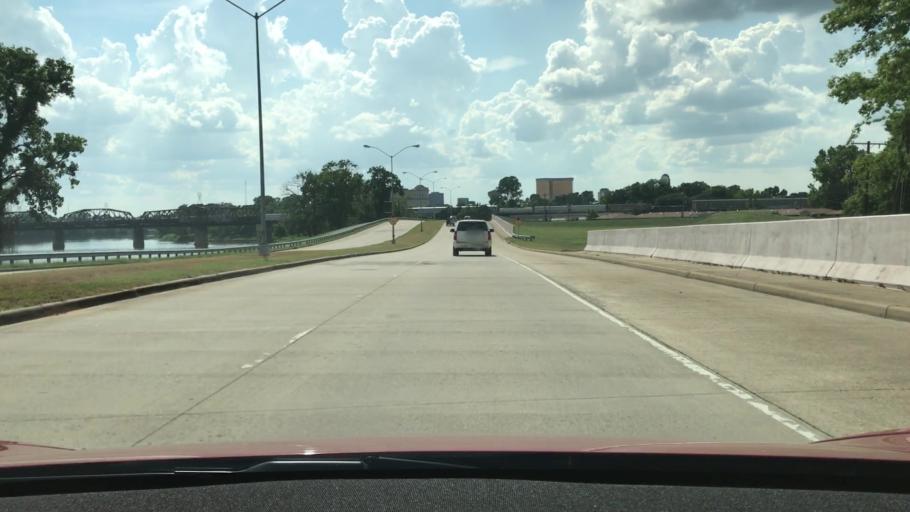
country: US
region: Louisiana
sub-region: Bossier Parish
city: Bossier City
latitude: 32.5098
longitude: -93.7185
